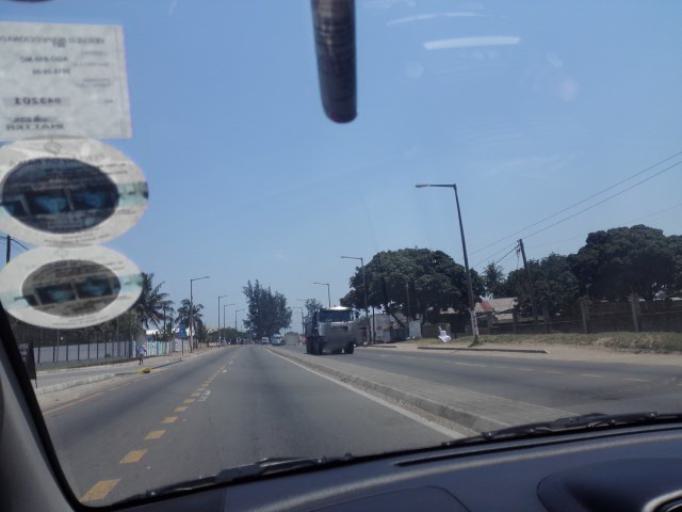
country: MZ
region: Maputo City
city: Maputo
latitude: -25.9002
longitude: 32.5645
